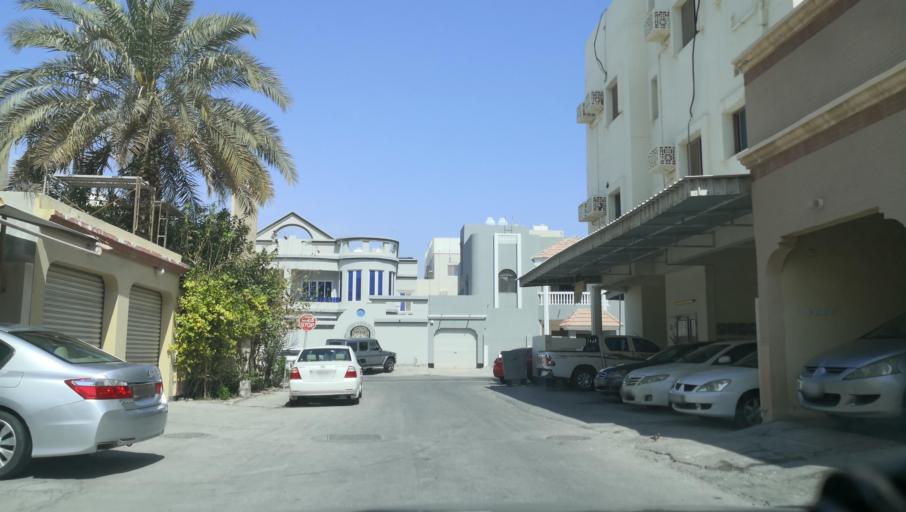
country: BH
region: Muharraq
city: Al Hadd
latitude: 26.2479
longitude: 50.6490
